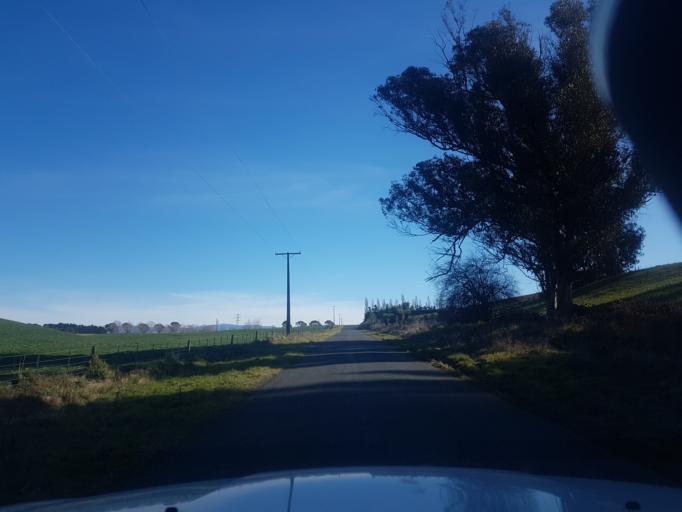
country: NZ
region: Canterbury
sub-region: Timaru District
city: Pleasant Point
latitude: -44.2515
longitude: 171.0586
